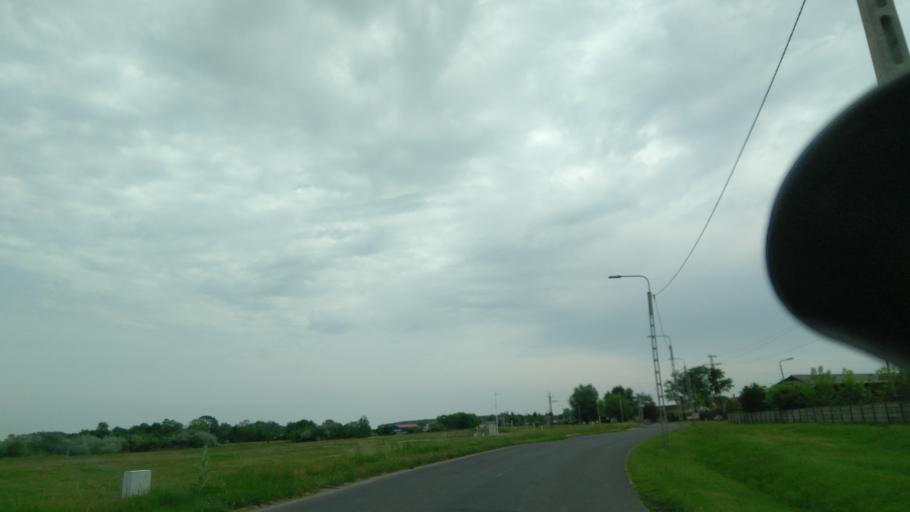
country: HU
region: Bekes
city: Szeghalom
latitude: 47.0326
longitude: 21.1741
